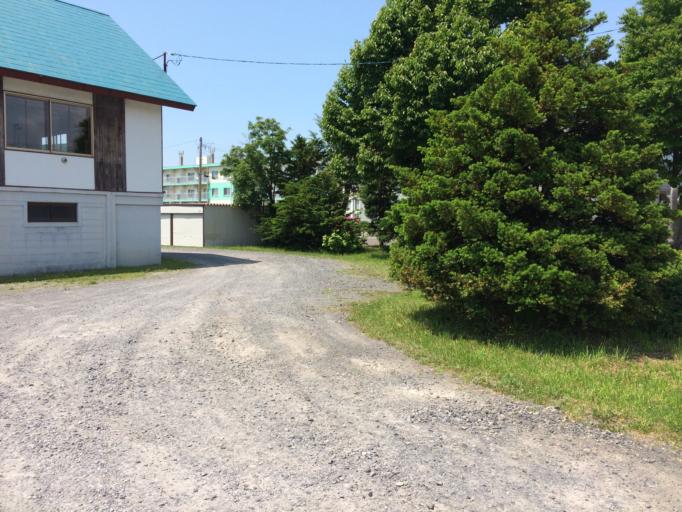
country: JP
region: Hokkaido
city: Niseko Town
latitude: 42.8978
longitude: 140.7521
